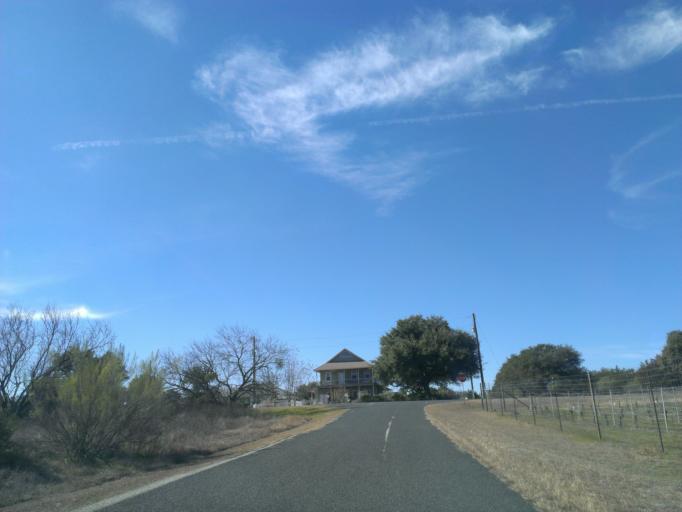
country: US
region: Texas
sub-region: Travis County
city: Briarcliff
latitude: 30.4357
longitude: -98.0666
